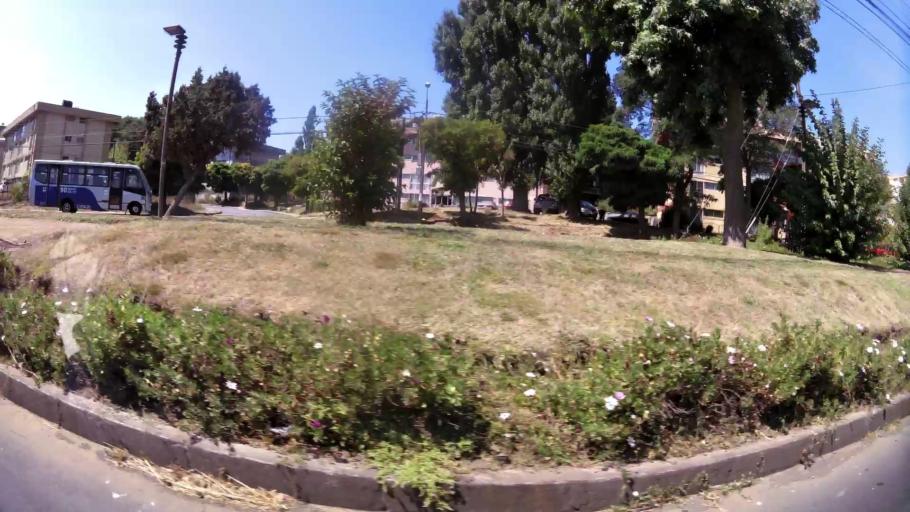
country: CL
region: Biobio
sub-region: Provincia de Concepcion
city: Concepcion
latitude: -36.8118
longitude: -73.0665
